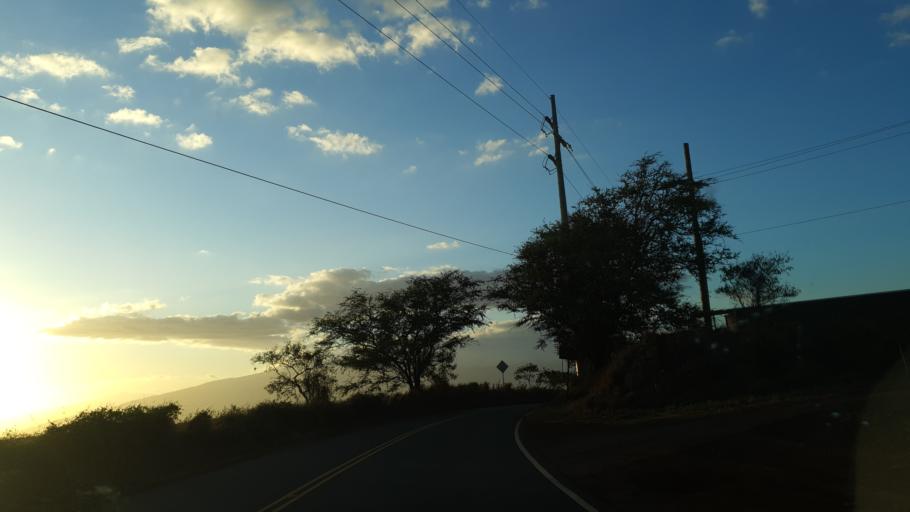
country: US
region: Hawaii
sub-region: Maui County
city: Pukalani
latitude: 20.7866
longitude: -156.3503
